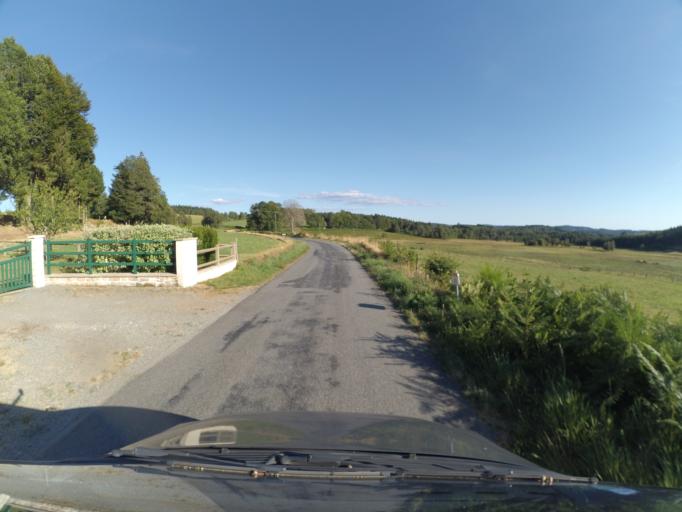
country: FR
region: Limousin
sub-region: Departement de la Creuse
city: Banize
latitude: 45.7344
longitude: 2.0400
